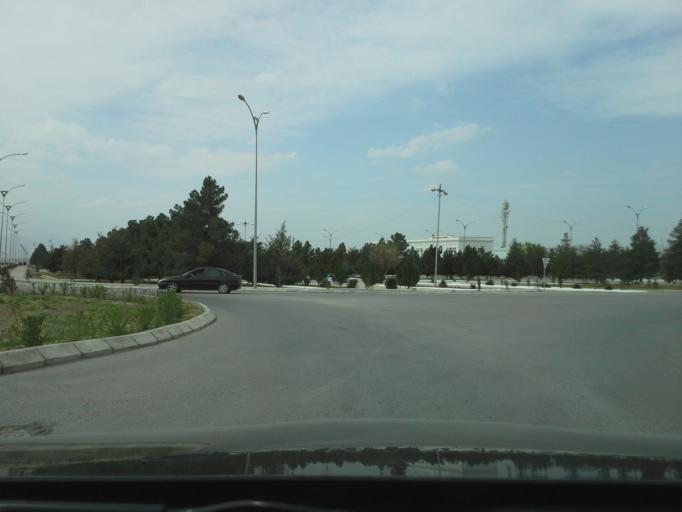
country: TM
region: Ahal
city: Abadan
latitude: 38.0552
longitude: 58.1496
